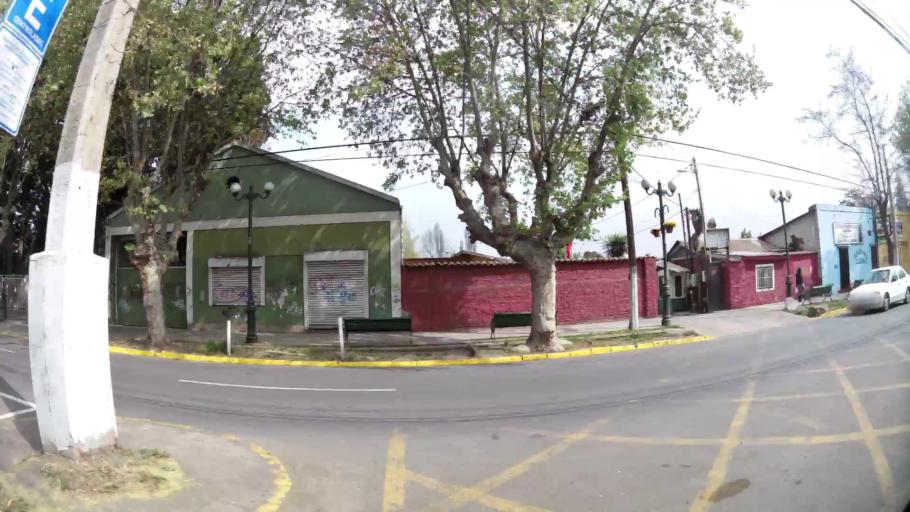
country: CL
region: Santiago Metropolitan
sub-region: Provincia de Chacabuco
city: Chicureo Abajo
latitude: -33.2040
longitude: -70.6787
